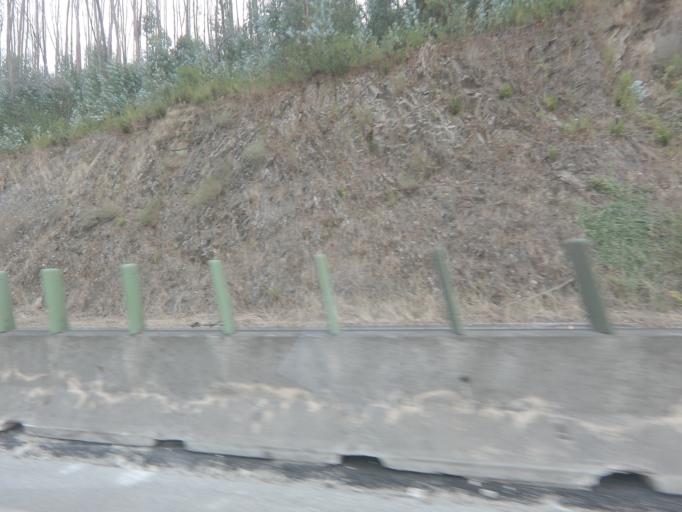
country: PT
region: Coimbra
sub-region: Penacova
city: Penacova
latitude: 40.2983
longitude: -8.2397
